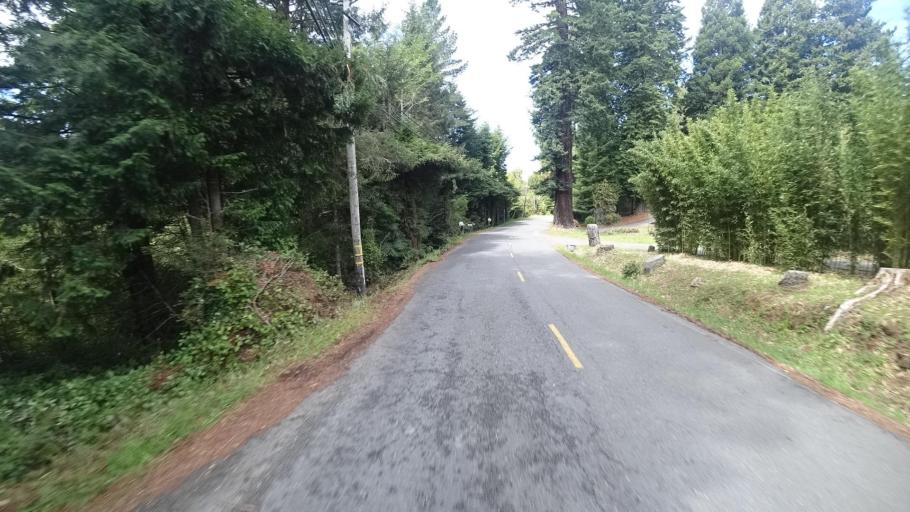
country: US
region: California
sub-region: Humboldt County
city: Bayside
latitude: 40.8666
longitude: -124.0503
